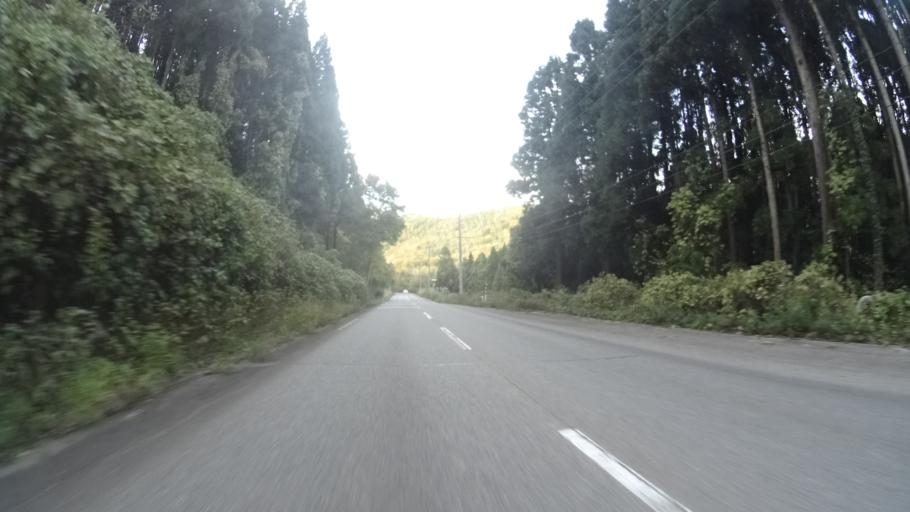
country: JP
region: Ishikawa
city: Nanao
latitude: 37.2134
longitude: 136.7066
